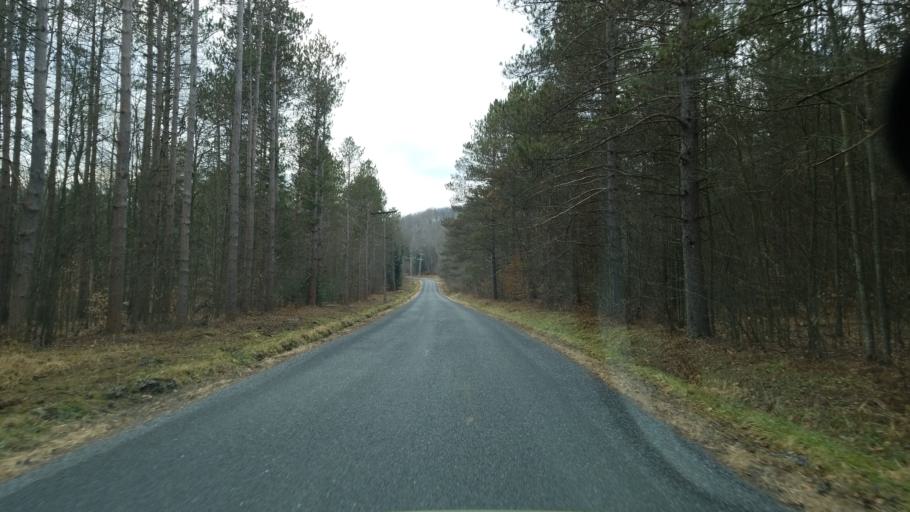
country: US
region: Pennsylvania
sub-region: Clearfield County
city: Treasure Lake
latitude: 41.1481
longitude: -78.5756
